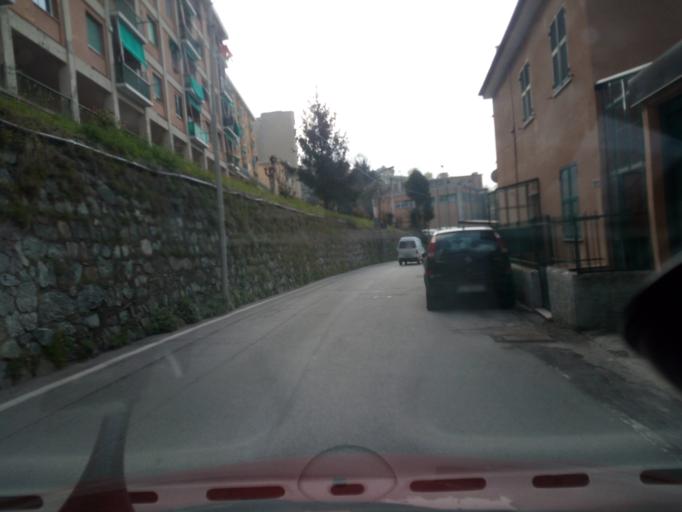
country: IT
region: Liguria
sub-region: Provincia di Genova
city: Mele
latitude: 44.4327
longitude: 8.7781
